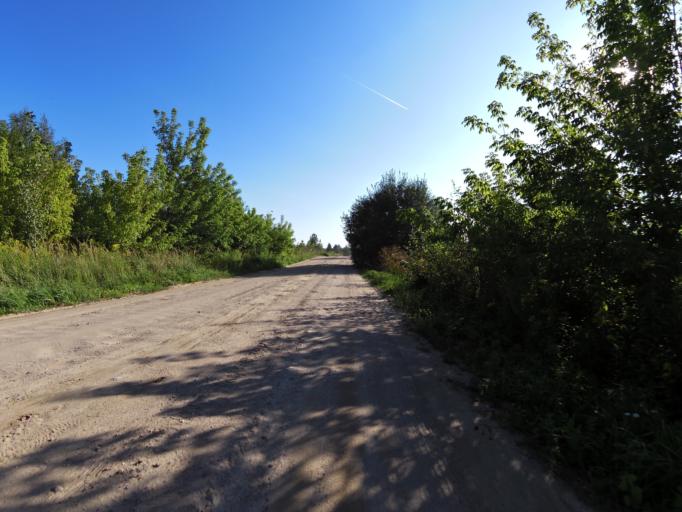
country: LT
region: Vilnius County
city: Pilaite
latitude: 54.7161
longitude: 25.1782
